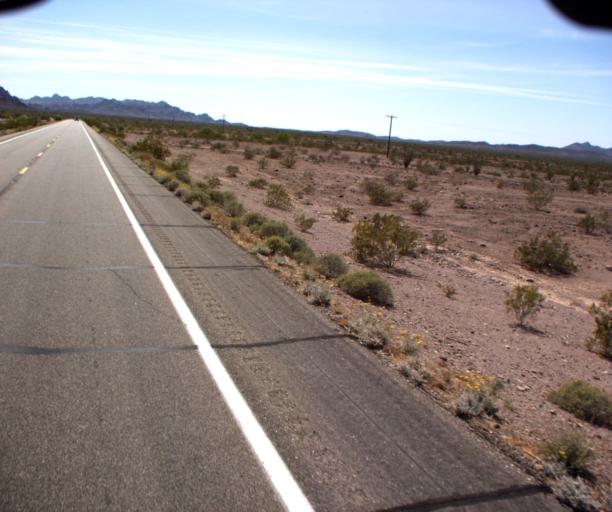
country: US
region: Arizona
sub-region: La Paz County
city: Quartzsite
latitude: 33.3157
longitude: -114.2169
